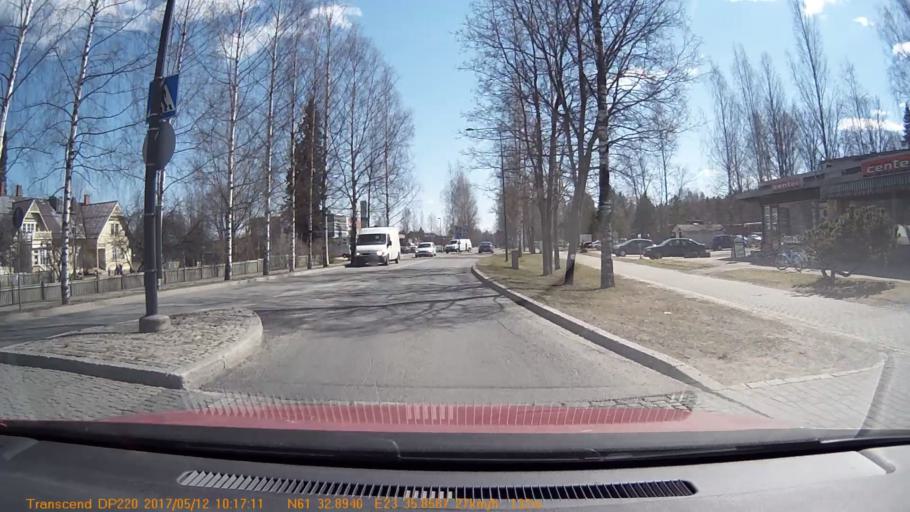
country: FI
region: Pirkanmaa
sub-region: Tampere
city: Yloejaervi
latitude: 61.5483
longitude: 23.5975
